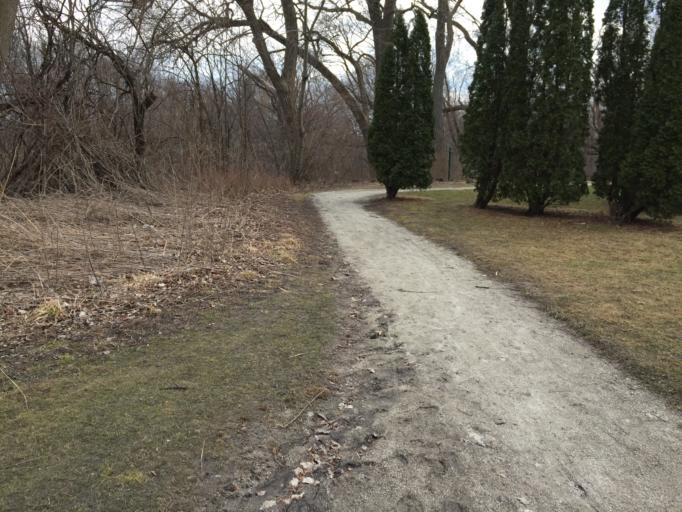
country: US
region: Illinois
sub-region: Cook County
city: Evanston
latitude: 42.0636
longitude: -87.6882
